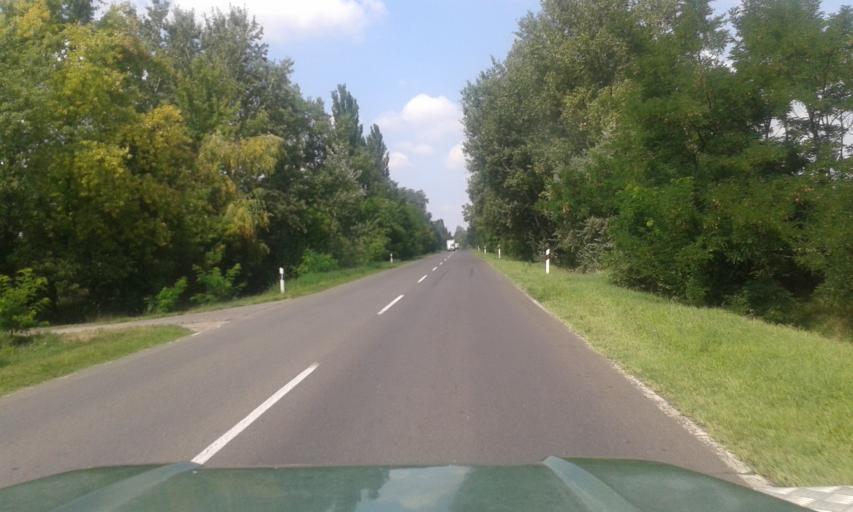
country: HU
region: Csongrad
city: Szatymaz
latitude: 46.3679
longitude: 20.0450
